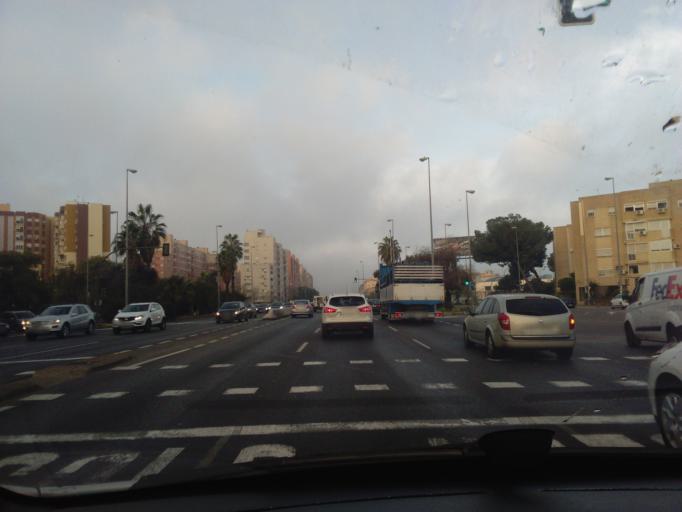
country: ES
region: Andalusia
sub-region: Provincia de Sevilla
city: Sevilla
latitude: 37.4176
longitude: -5.9647
